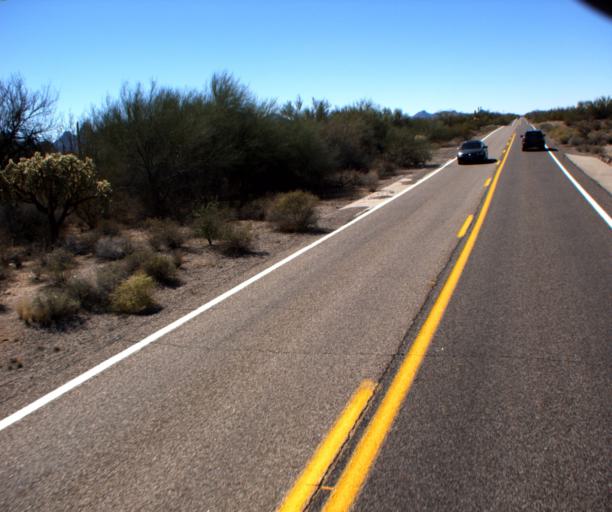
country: US
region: Arizona
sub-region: Pima County
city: Ajo
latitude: 32.1857
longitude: -112.7611
